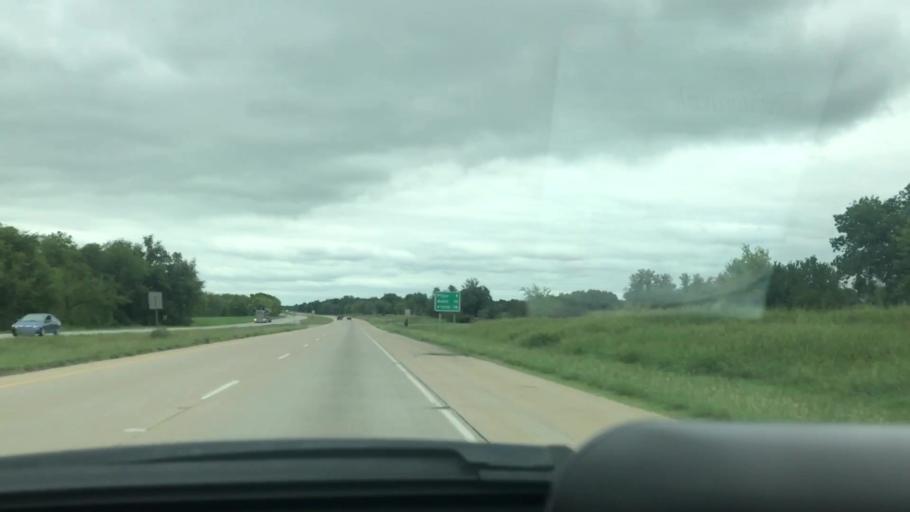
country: US
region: Oklahoma
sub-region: Mayes County
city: Chouteau
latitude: 36.1969
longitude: -95.3413
